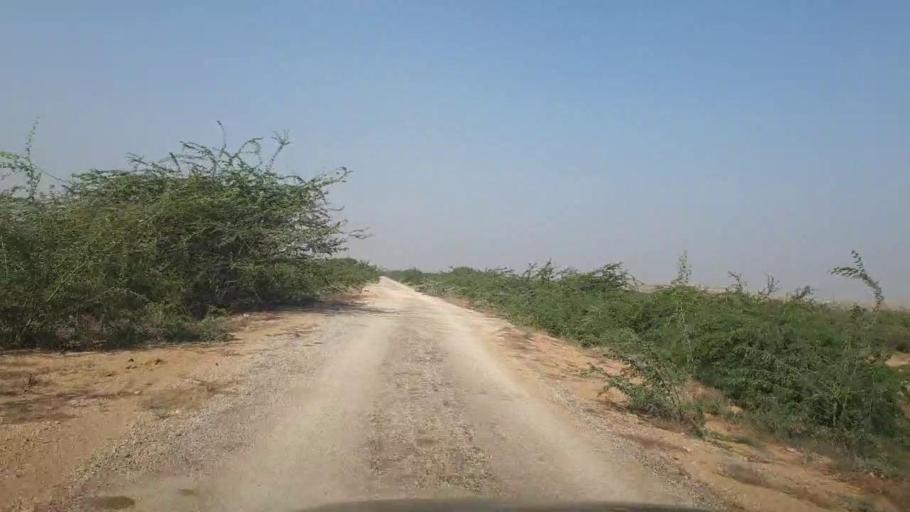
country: PK
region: Sindh
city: Gharo
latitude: 25.0515
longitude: 67.5556
